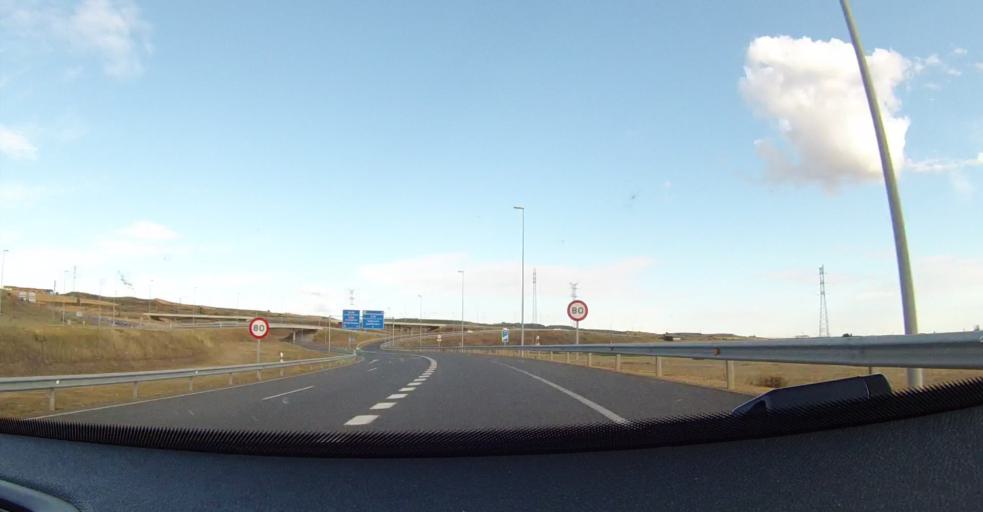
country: ES
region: Castille and Leon
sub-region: Provincia de Leon
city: Leon
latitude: 42.5717
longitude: -5.5483
